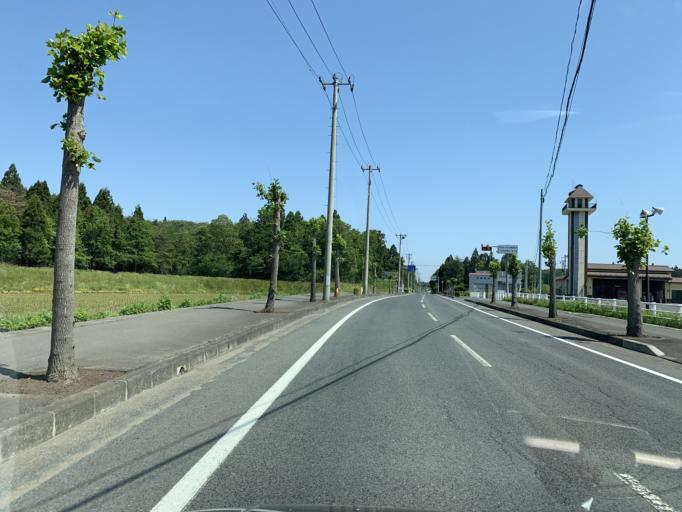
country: JP
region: Iwate
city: Kitakami
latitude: 39.2077
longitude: 141.0948
